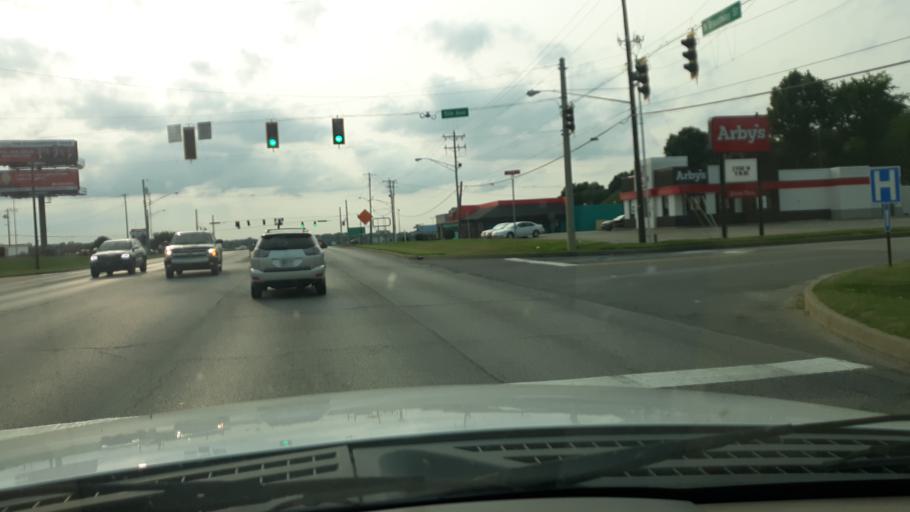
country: US
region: Indiana
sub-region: Gibson County
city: Princeton
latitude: 38.3555
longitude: -87.5912
